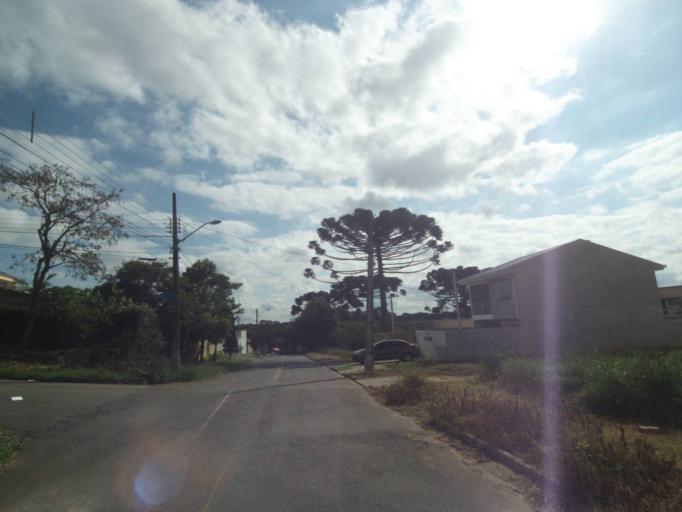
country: BR
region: Parana
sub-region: Curitiba
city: Curitiba
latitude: -25.3823
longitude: -49.2963
